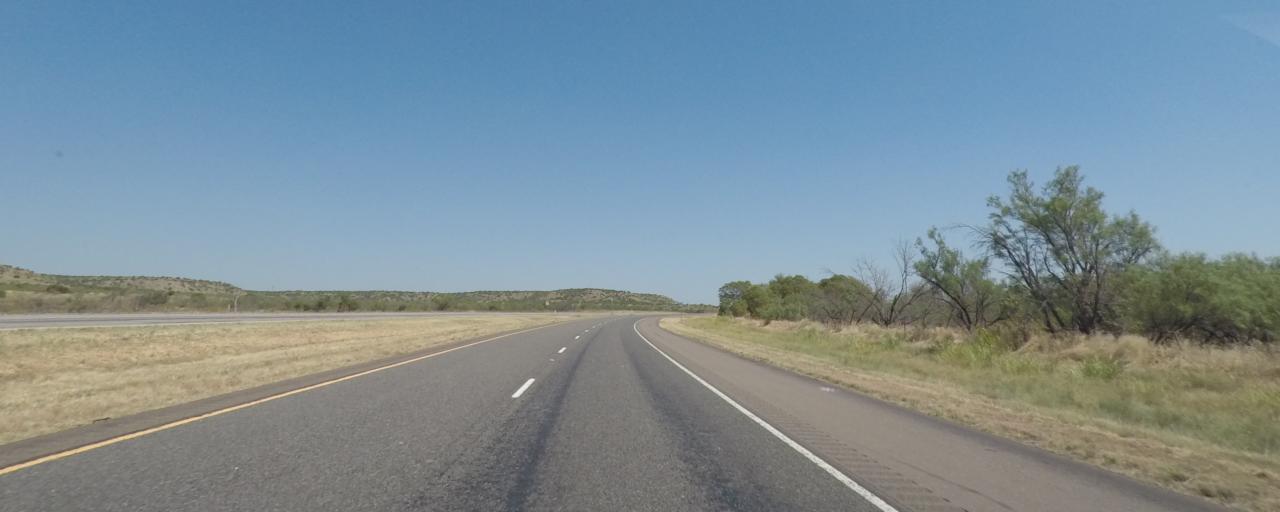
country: US
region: Texas
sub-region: Dickens County
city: Dickens
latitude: 33.6331
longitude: -100.8816
